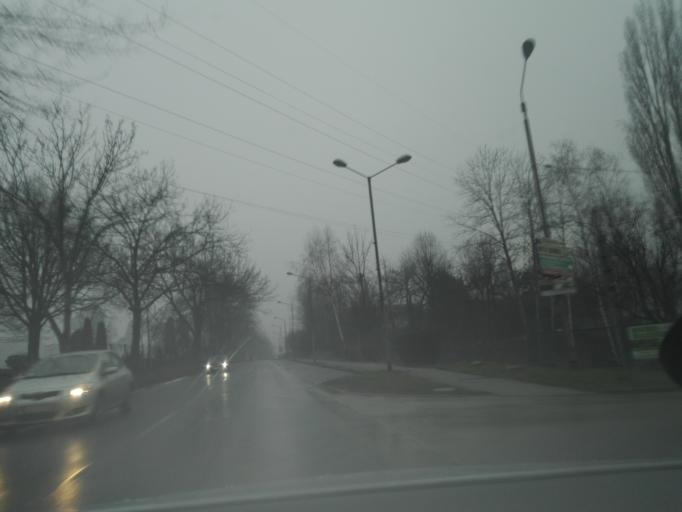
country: PL
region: Silesian Voivodeship
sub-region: Katowice
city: Katowice
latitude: 50.2716
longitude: 19.0454
